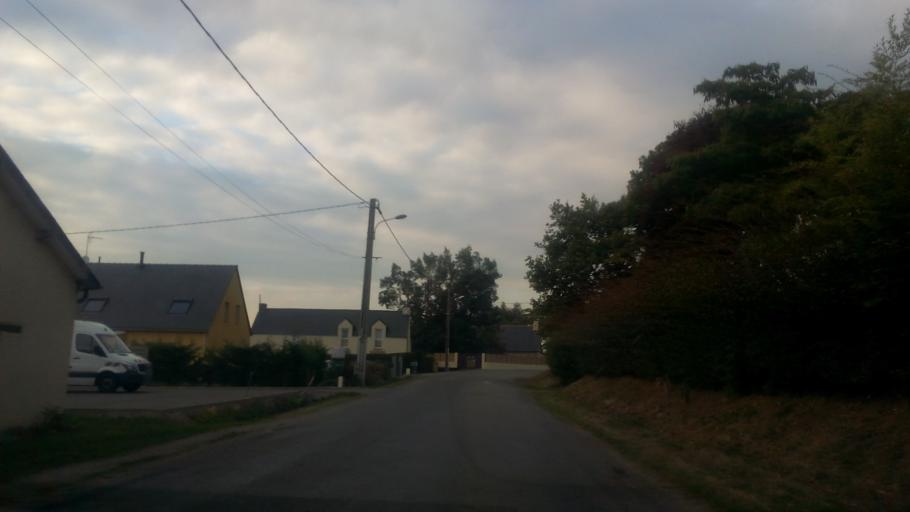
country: FR
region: Brittany
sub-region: Departement du Morbihan
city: Peillac
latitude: 47.7100
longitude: -2.2149
